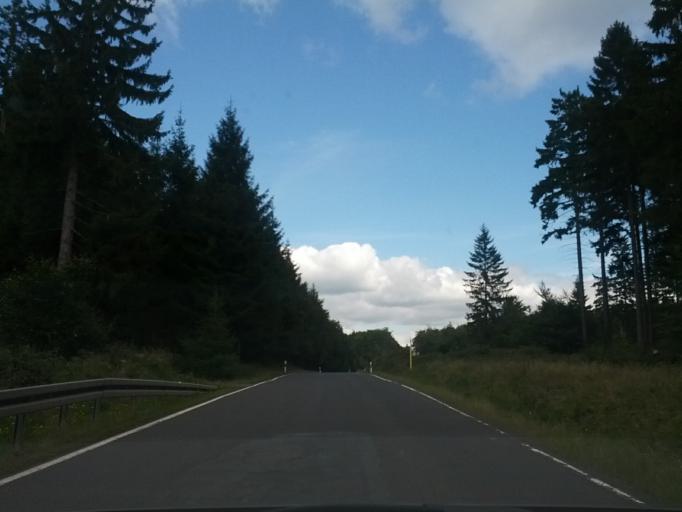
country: DE
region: Thuringia
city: Ruhla
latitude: 50.8642
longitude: 10.4033
